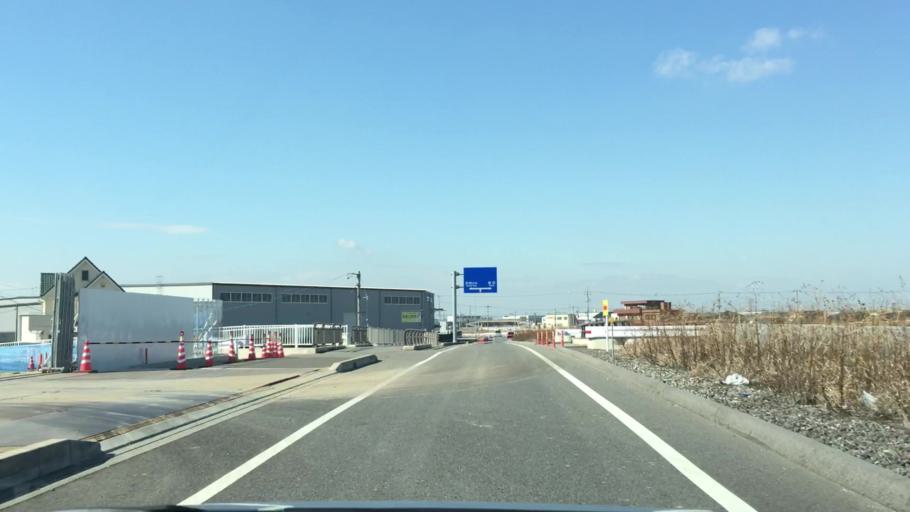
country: JP
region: Aichi
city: Anjo
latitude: 34.9937
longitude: 137.1134
